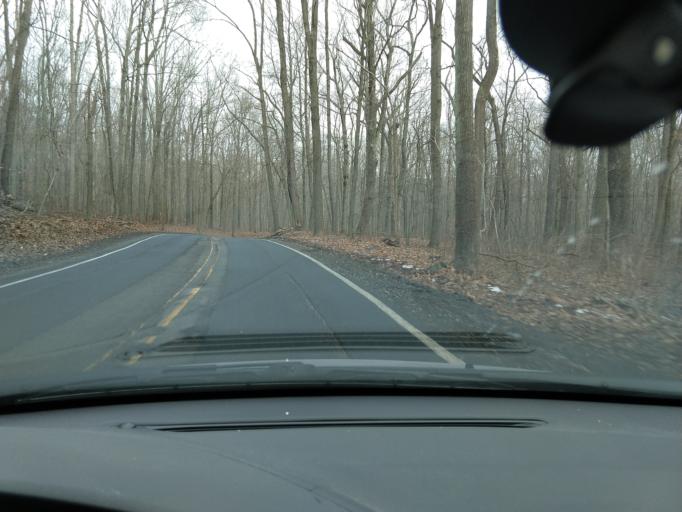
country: US
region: Pennsylvania
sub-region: Chester County
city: Elverson
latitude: 40.1979
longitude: -75.7730
